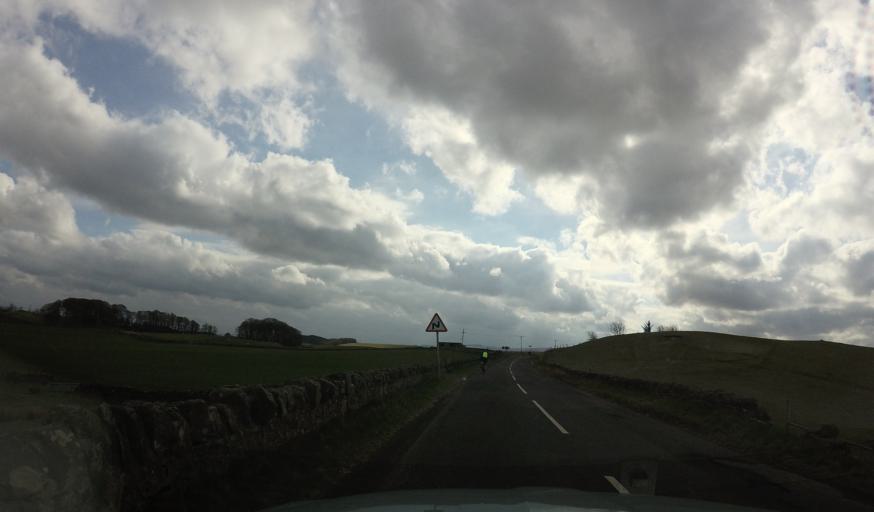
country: GB
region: Scotland
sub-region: Midlothian
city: Penicuik
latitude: 55.7992
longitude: -3.1574
